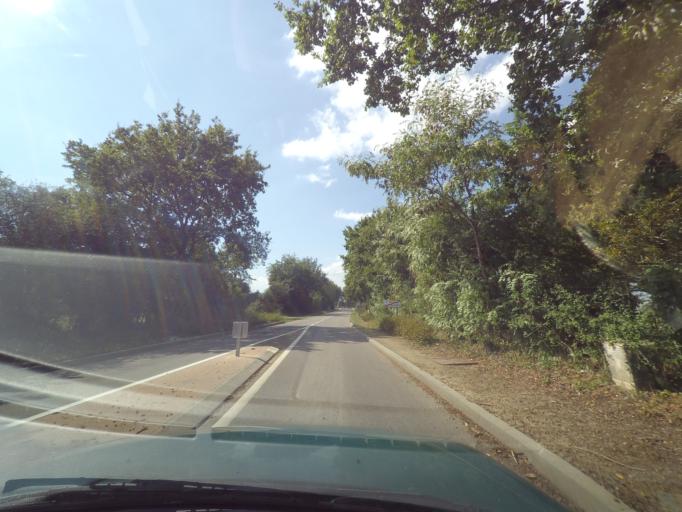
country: FR
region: Pays de la Loire
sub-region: Departement de la Loire-Atlantique
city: Saint-Hilaire-de-Chaleons
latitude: 47.1053
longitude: -1.8738
